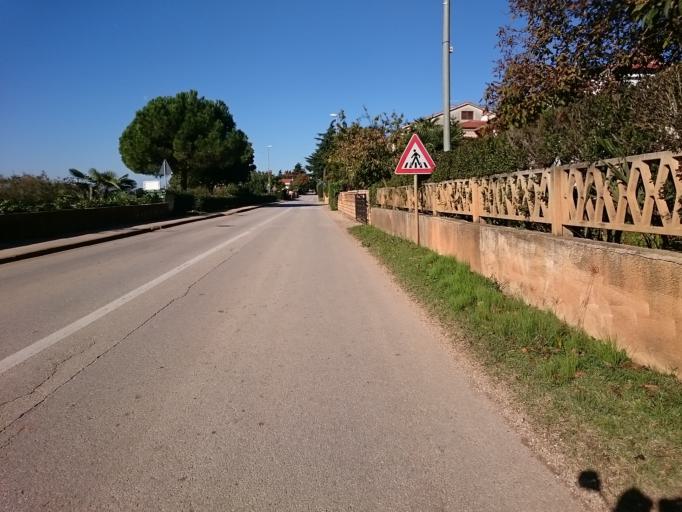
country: HR
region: Istarska
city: Novigrad
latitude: 45.3593
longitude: 13.5554
